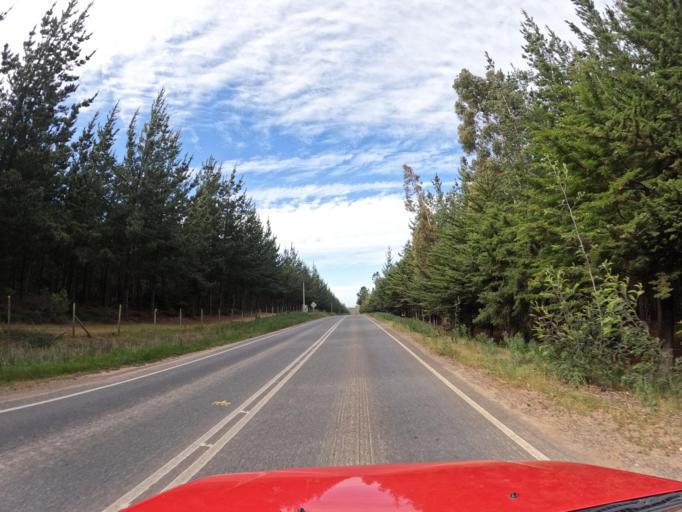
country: CL
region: O'Higgins
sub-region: Provincia de Colchagua
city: Santa Cruz
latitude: -34.3212
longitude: -71.8681
